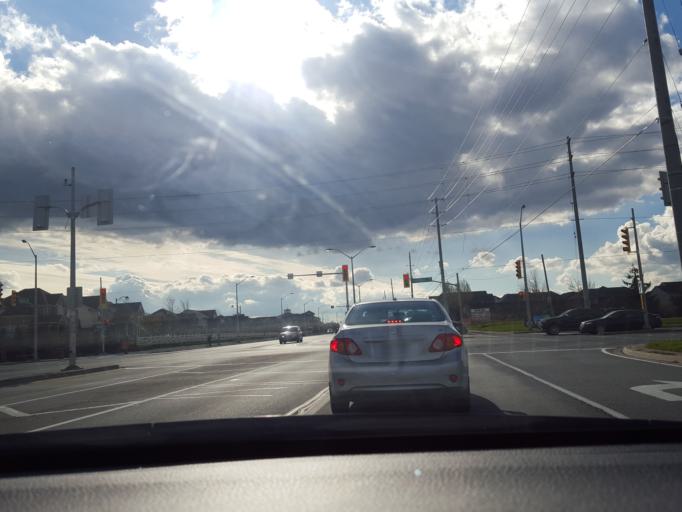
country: CA
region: Ontario
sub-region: Halton
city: Milton
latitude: 43.5312
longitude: -79.8348
